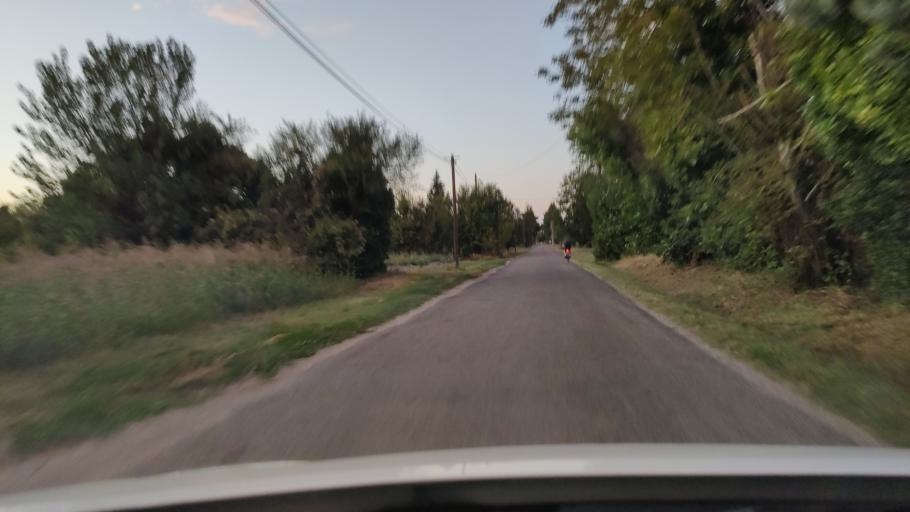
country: FR
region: Provence-Alpes-Cote d'Azur
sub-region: Departement du Vaucluse
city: Le Thor
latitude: 43.9537
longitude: 4.9711
